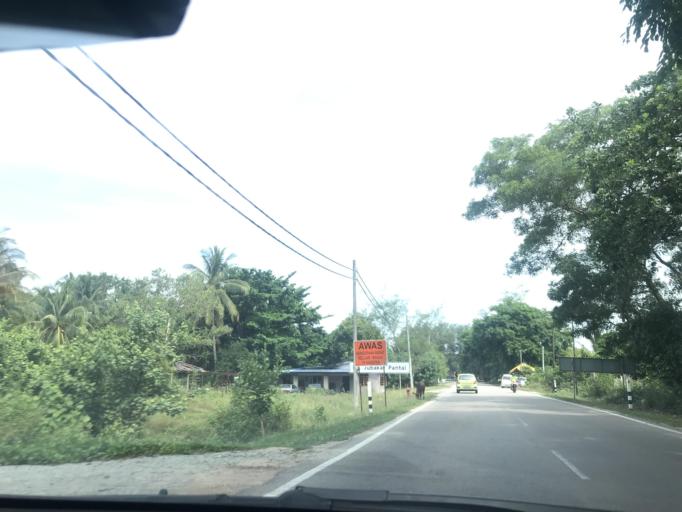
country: MY
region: Kelantan
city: Tumpat
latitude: 6.2059
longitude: 102.1470
